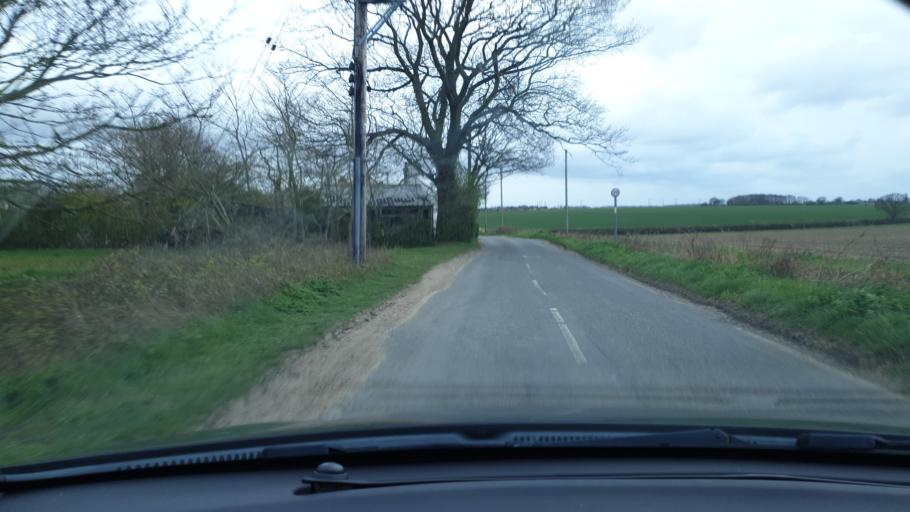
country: GB
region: England
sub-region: Essex
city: Mistley
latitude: 51.9363
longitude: 1.1748
